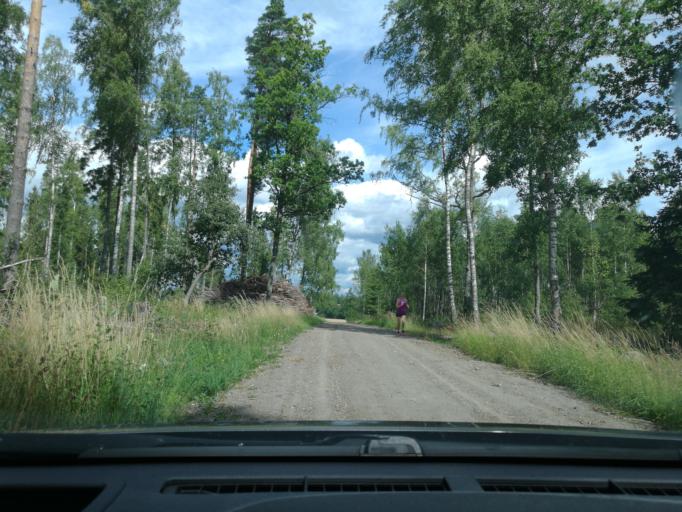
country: SE
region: Stockholm
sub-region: Sigtuna Kommun
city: Marsta
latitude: 59.6076
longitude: 17.8014
